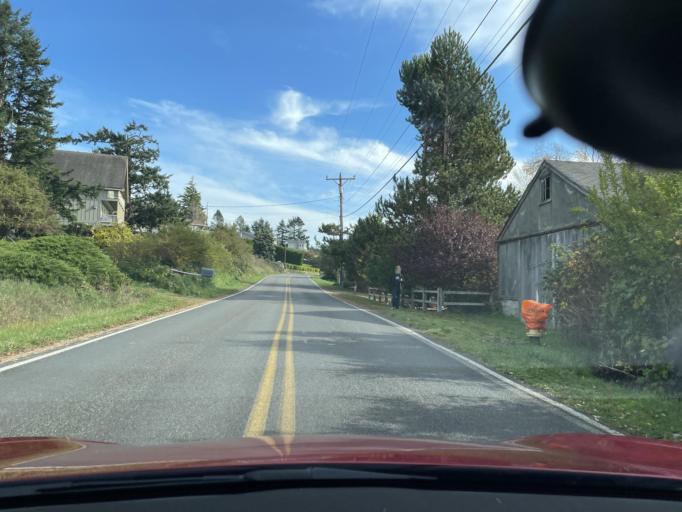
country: US
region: Washington
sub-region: San Juan County
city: Friday Harbor
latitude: 48.5223
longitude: -123.0130
